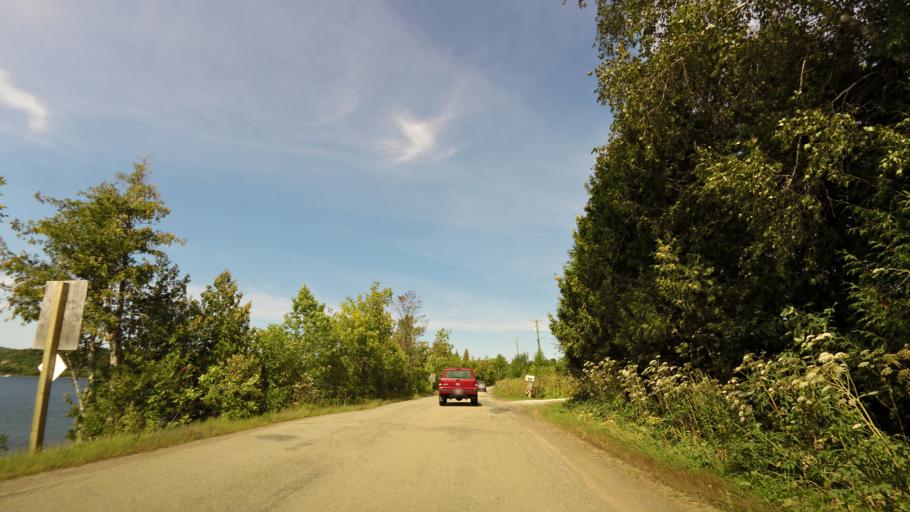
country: CA
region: New Brunswick
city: Hampton
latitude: 45.6035
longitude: -65.9084
